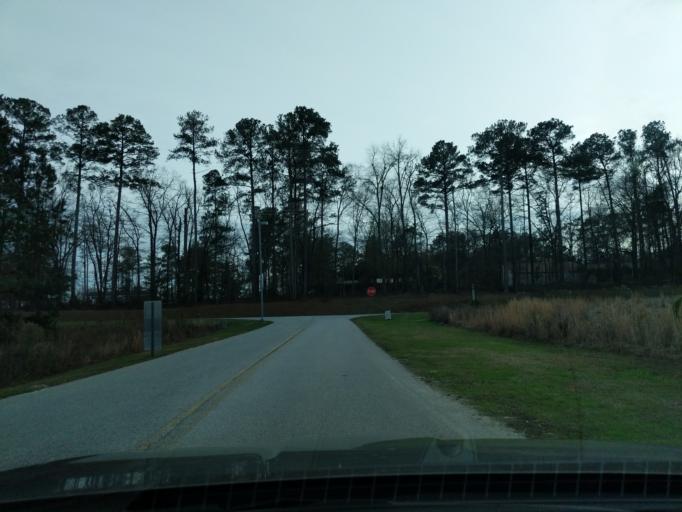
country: US
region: Georgia
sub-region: Columbia County
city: Grovetown
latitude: 33.4646
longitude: -82.1948
